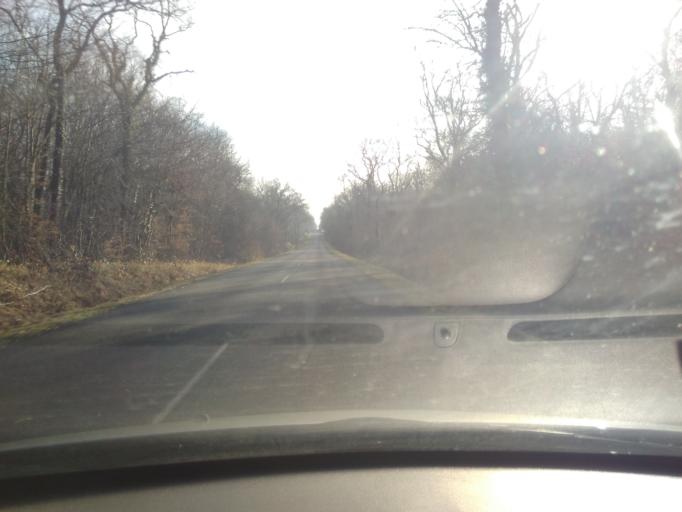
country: FR
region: Bourgogne
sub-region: Departement de la Nievre
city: Saint-Parize-le-Chatel
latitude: 46.8080
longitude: 3.2655
